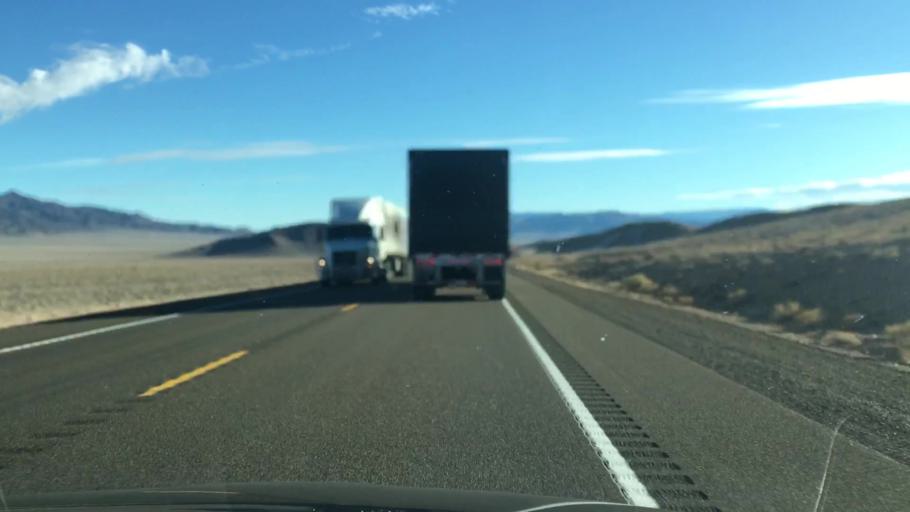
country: US
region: Nevada
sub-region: Nye County
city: Tonopah
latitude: 38.1643
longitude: -117.9535
